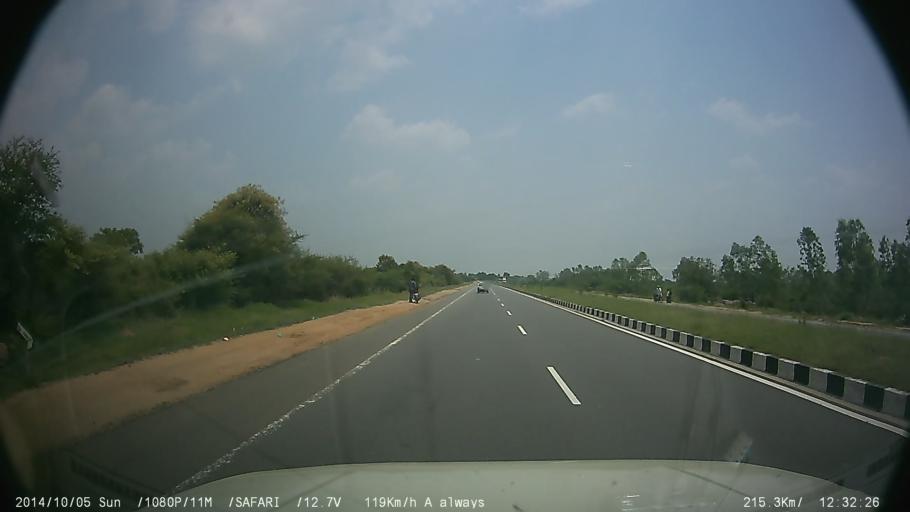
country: IN
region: Tamil Nadu
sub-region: Cuddalore
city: Vriddhachalam
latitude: 11.7122
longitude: 79.2155
